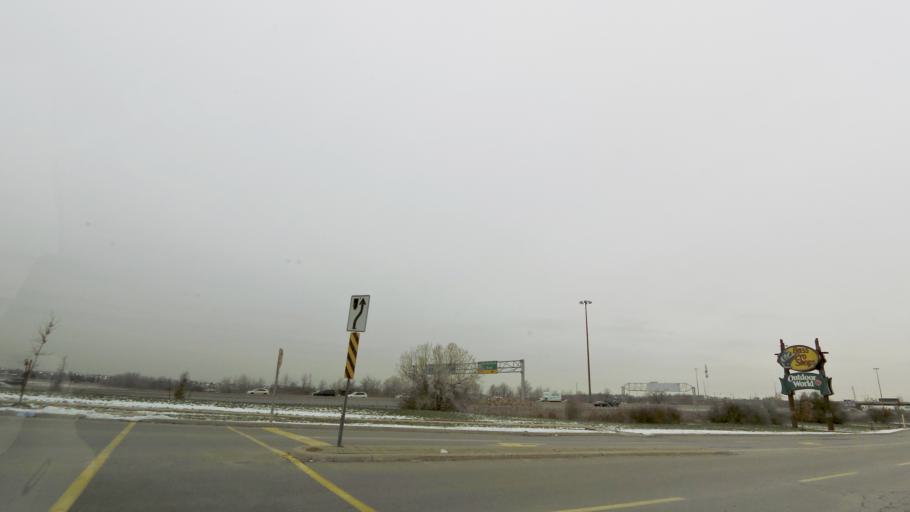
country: CA
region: Ontario
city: Vaughan
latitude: 43.8232
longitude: -79.5448
